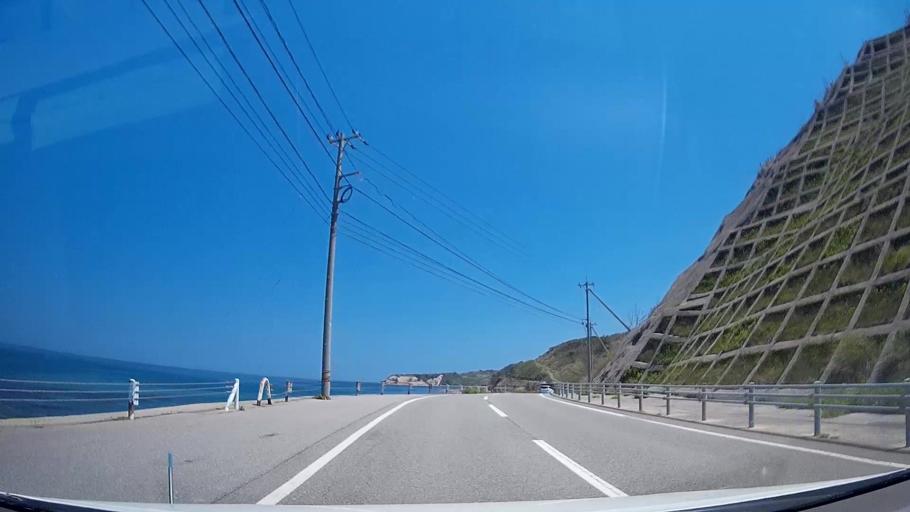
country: JP
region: Ishikawa
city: Nanao
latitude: 37.4347
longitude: 137.0323
